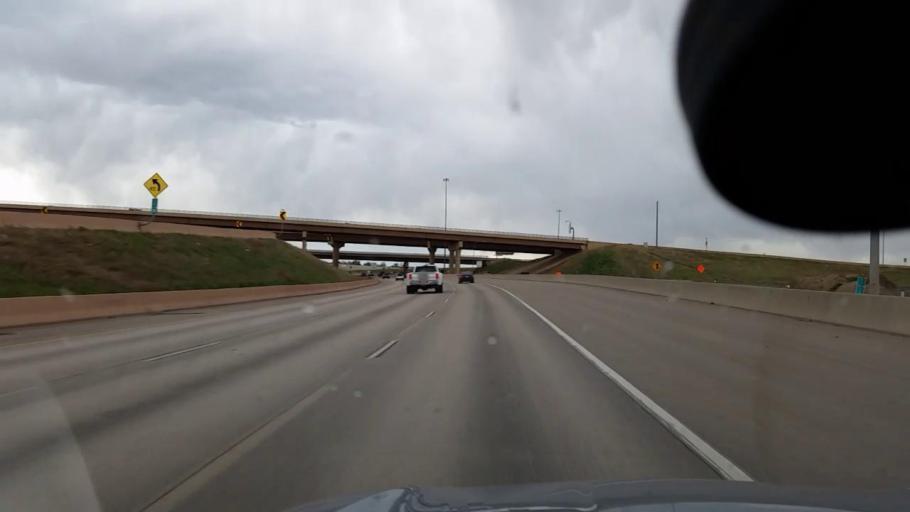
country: US
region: Colorado
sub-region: Adams County
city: Twin Lakes
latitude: 39.8250
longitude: -104.9816
